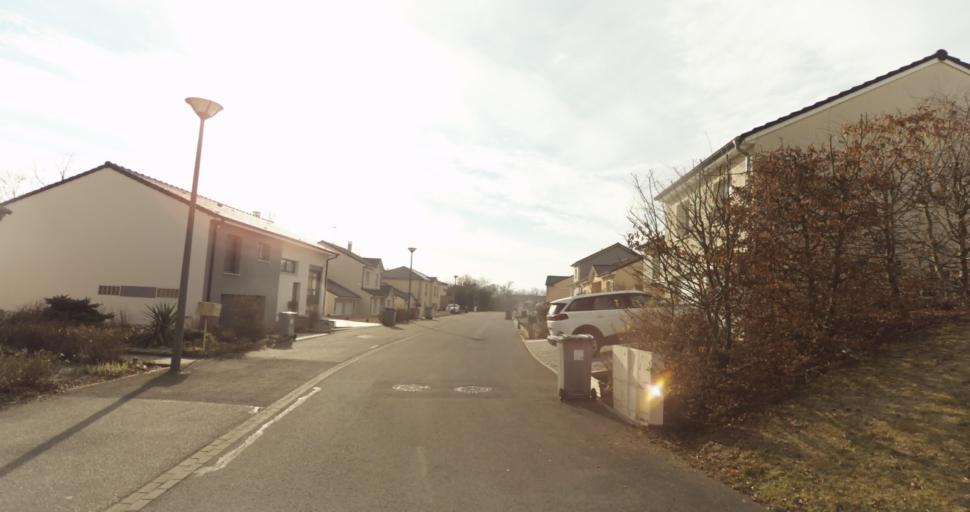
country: FR
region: Lorraine
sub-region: Departement de Meurthe-et-Moselle
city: Jarny
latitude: 49.1626
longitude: 5.8848
